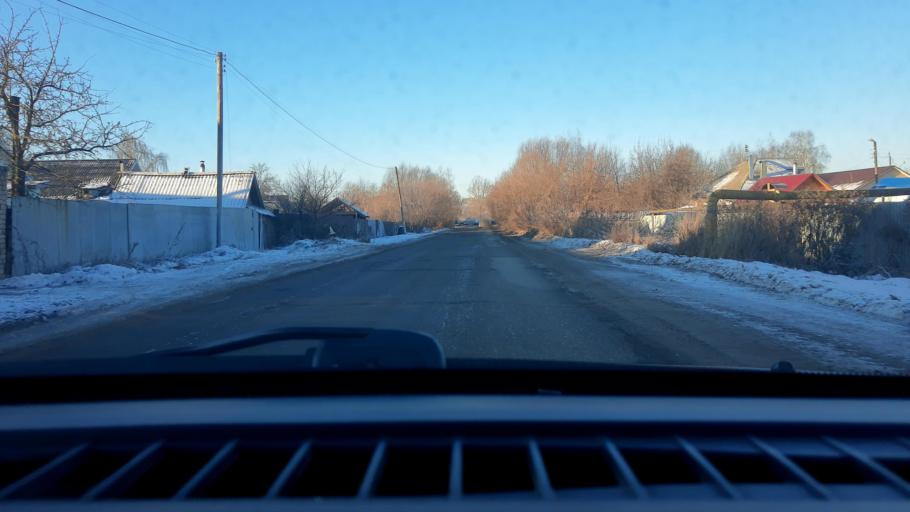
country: RU
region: Nizjnij Novgorod
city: Bor
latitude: 56.3676
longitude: 44.0952
